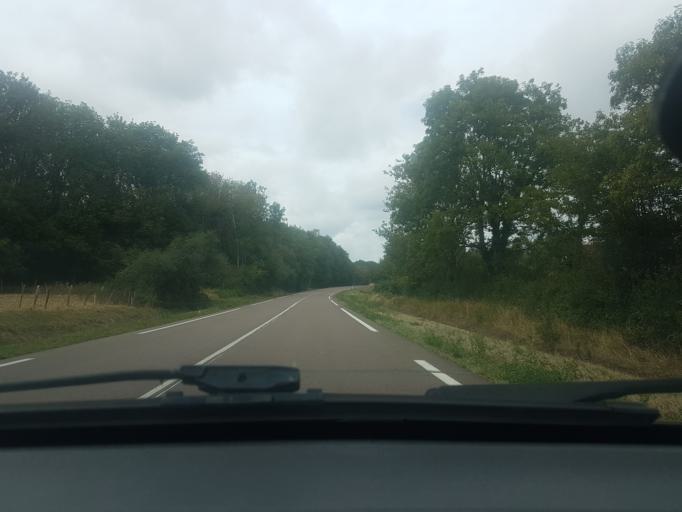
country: FR
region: Bourgogne
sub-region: Departement de la Cote-d'Or
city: Saulieu
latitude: 47.2127
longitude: 4.3522
